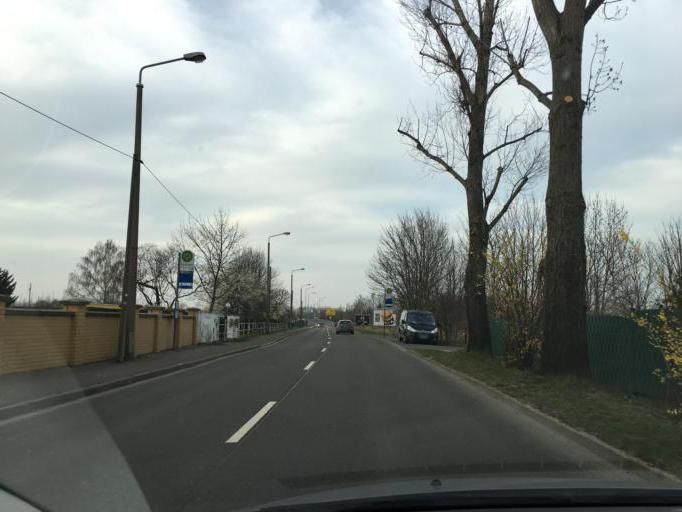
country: DE
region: Saxony
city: Taucha
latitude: 51.3556
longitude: 12.4443
